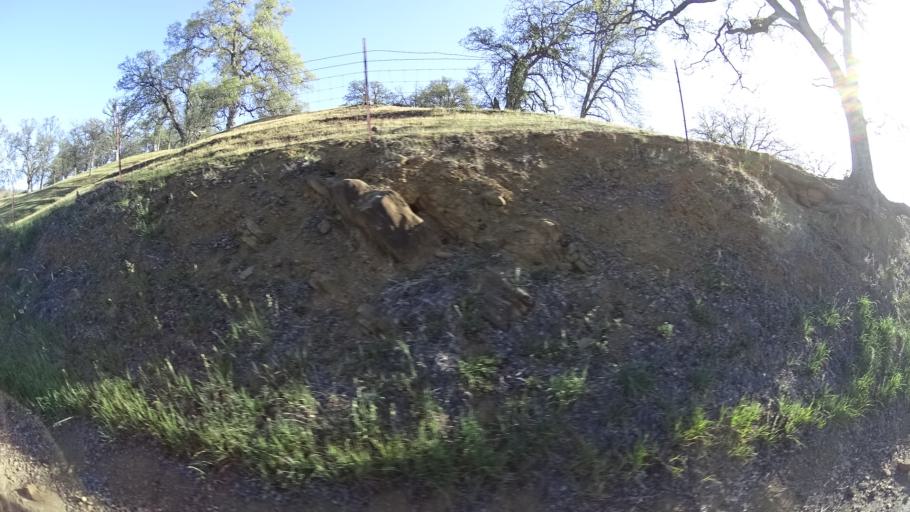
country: US
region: California
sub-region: Tehama County
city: Rancho Tehama Reserve
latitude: 39.7874
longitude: -122.4834
